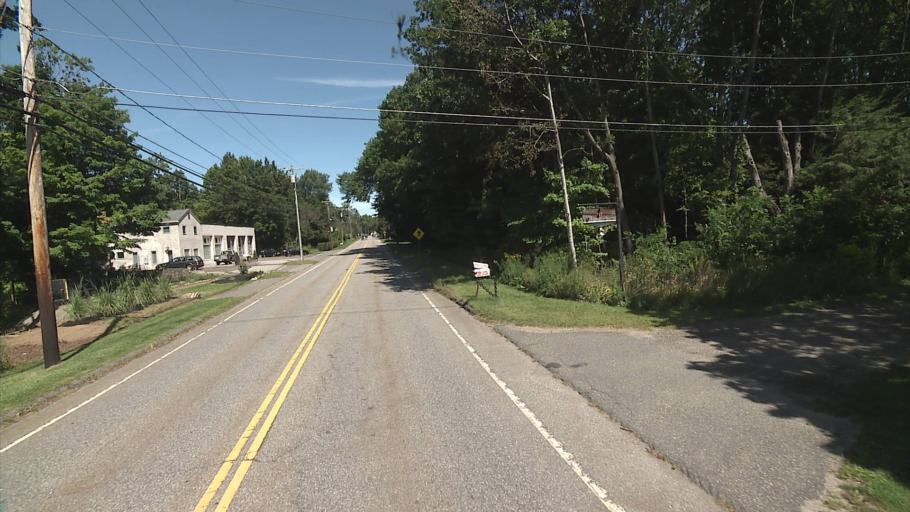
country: US
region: Connecticut
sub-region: Litchfield County
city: Litchfield
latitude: 41.7069
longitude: -73.2347
